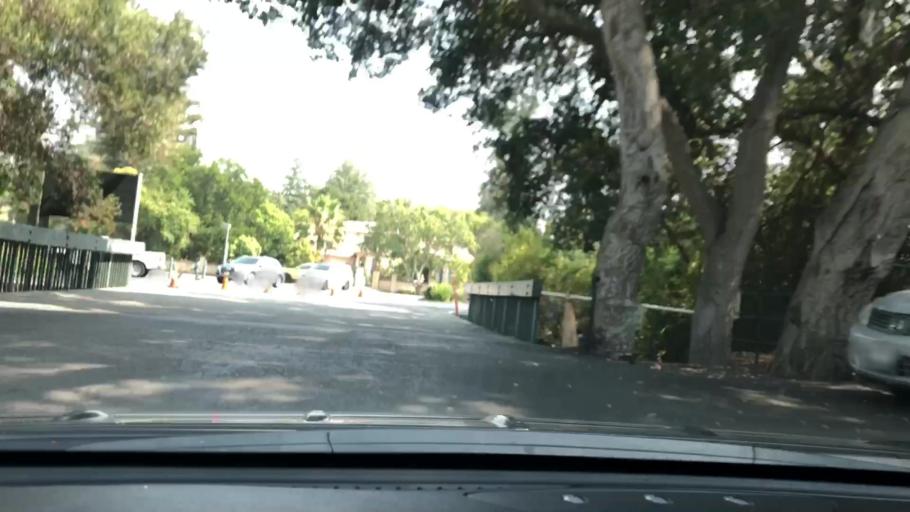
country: US
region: California
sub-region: Santa Clara County
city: Loyola
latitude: 37.3590
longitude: -122.1000
